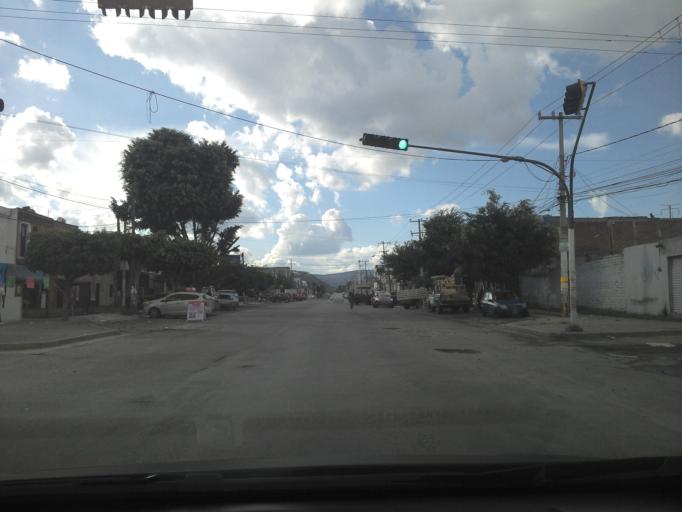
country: MX
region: Jalisco
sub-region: Tlajomulco de Zuniga
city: La Tijera
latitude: 20.6136
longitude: -103.4339
